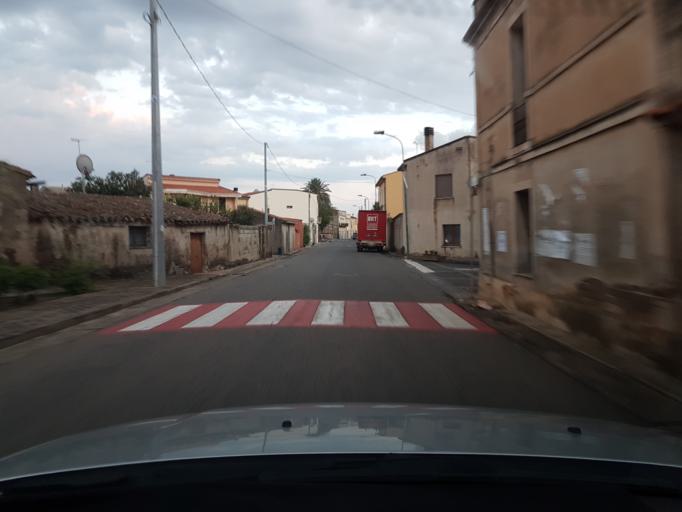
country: IT
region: Sardinia
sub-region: Provincia di Oristano
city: Tramatza
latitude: 40.0048
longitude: 8.6483
